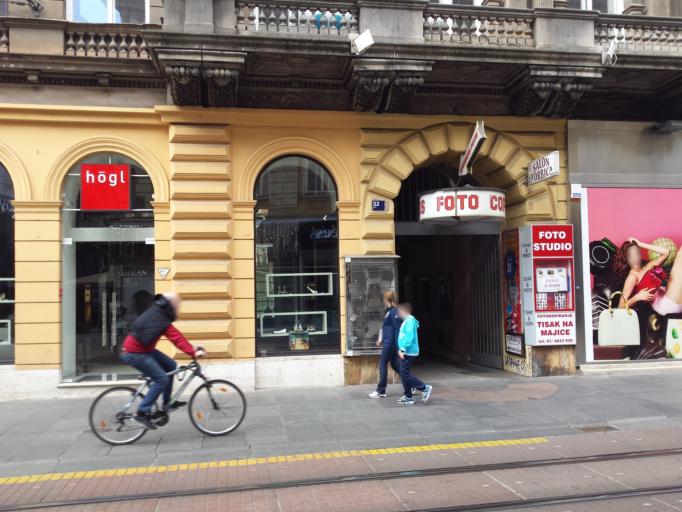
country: HR
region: Grad Zagreb
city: Zagreb - Centar
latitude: 45.8131
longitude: 15.9740
